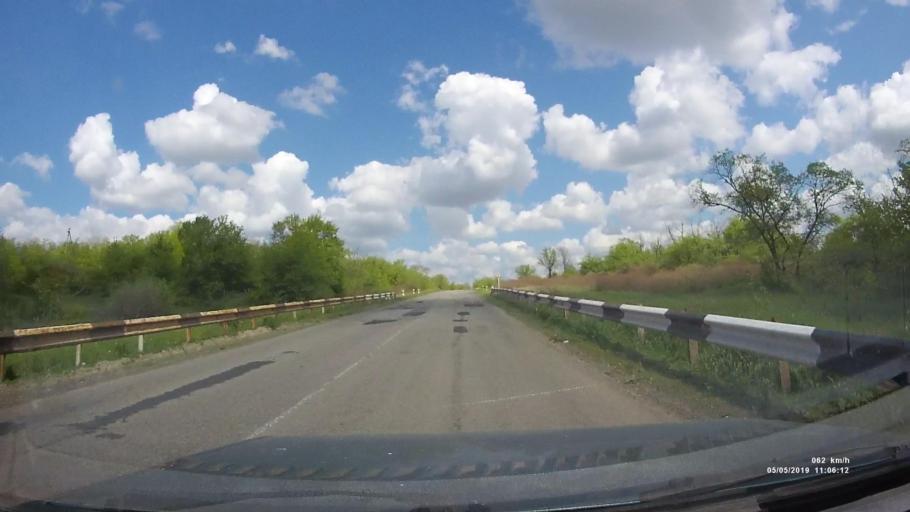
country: RU
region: Rostov
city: Ust'-Donetskiy
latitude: 47.7131
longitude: 40.9111
